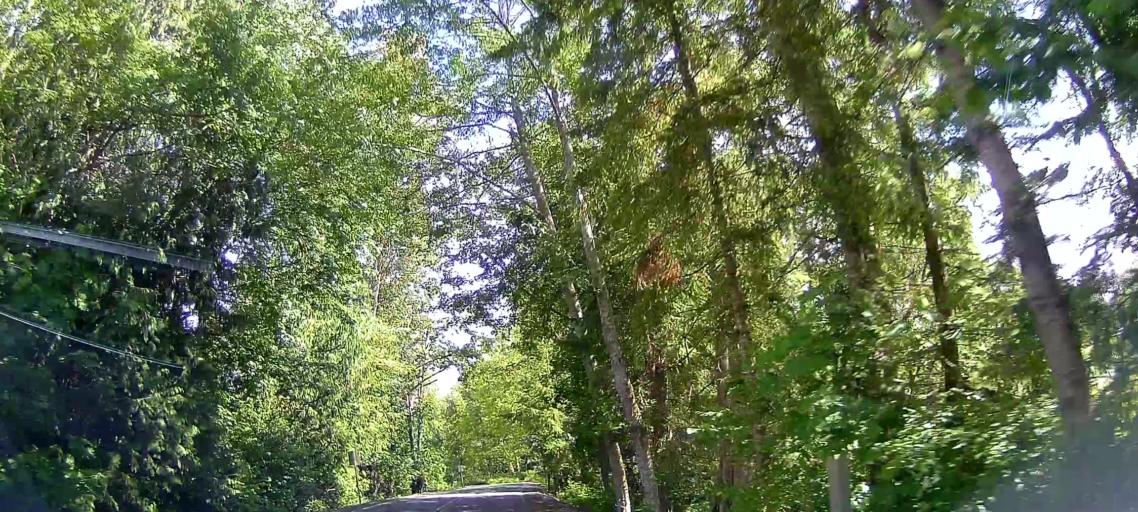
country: US
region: Washington
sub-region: Skagit County
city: Sedro-Woolley
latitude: 48.5304
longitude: -122.2173
